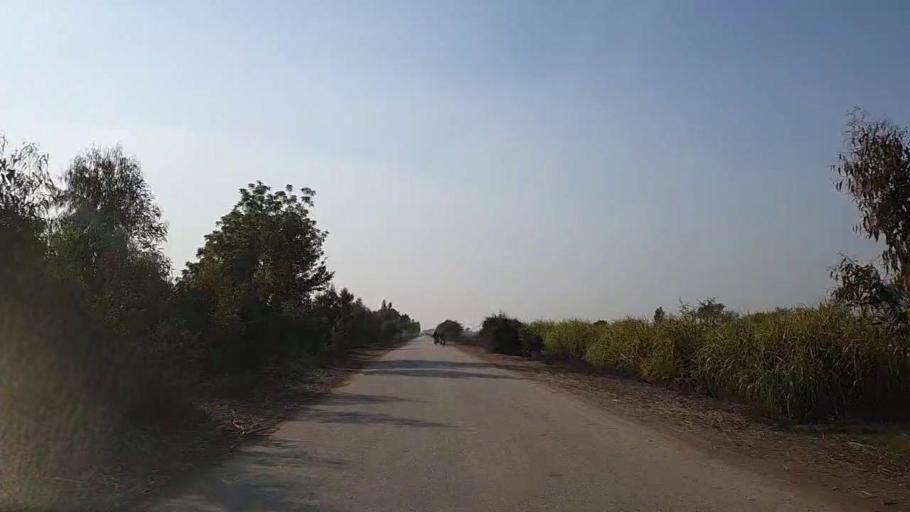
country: PK
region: Sindh
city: Daur
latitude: 26.4040
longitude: 68.2782
